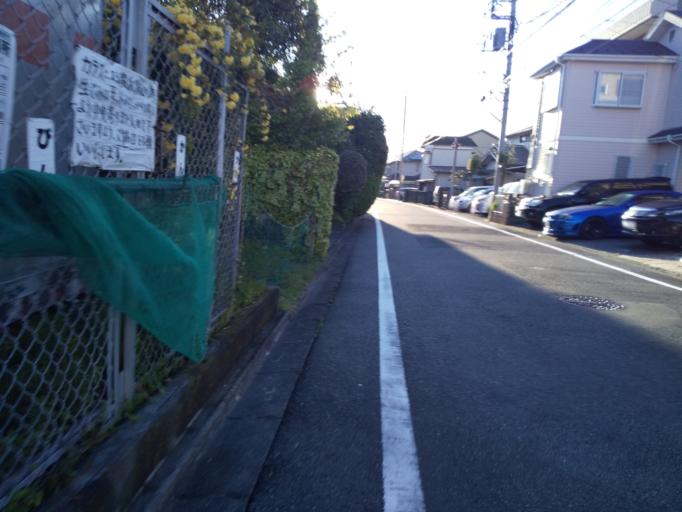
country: JP
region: Kanagawa
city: Zama
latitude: 35.5628
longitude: 139.3746
